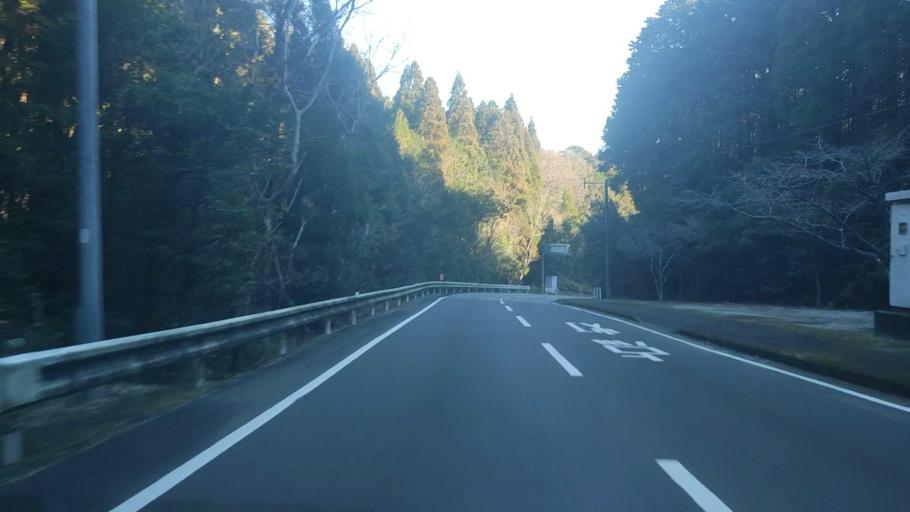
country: JP
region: Miyazaki
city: Nobeoka
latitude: 32.6755
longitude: 131.7730
